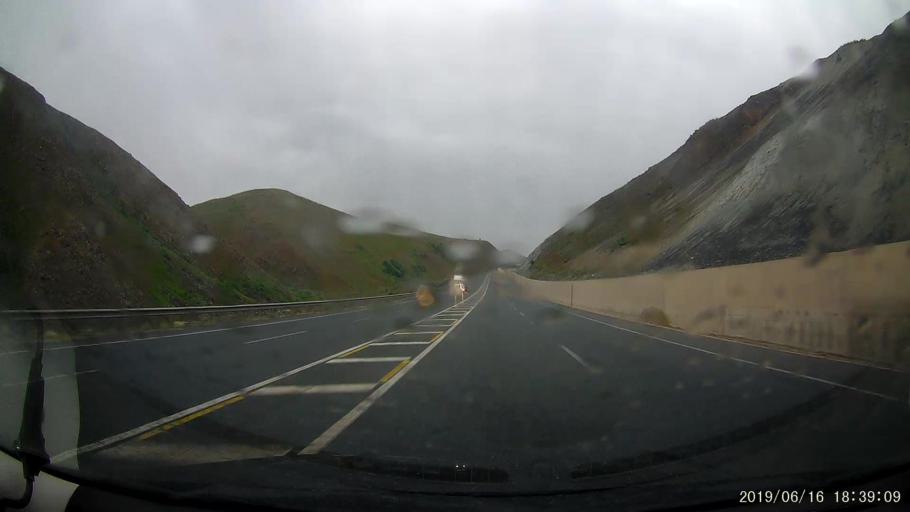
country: TR
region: Erzincan
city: Catalarmut
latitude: 39.8827
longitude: 39.1711
